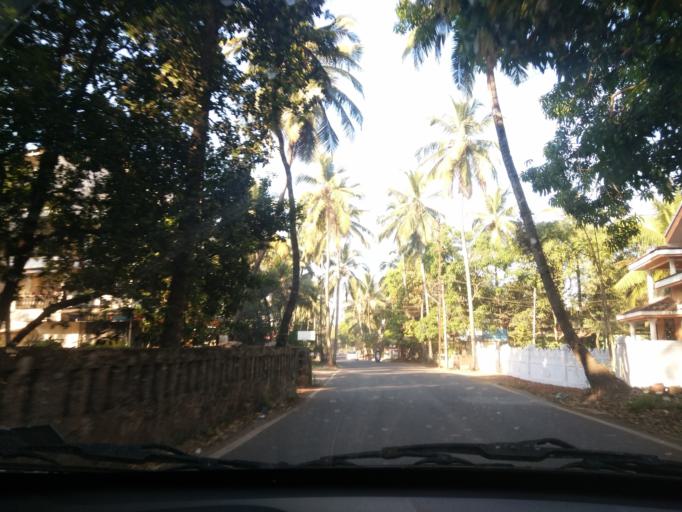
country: IN
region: Goa
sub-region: South Goa
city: Madgaon
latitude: 15.2549
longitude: 73.9632
